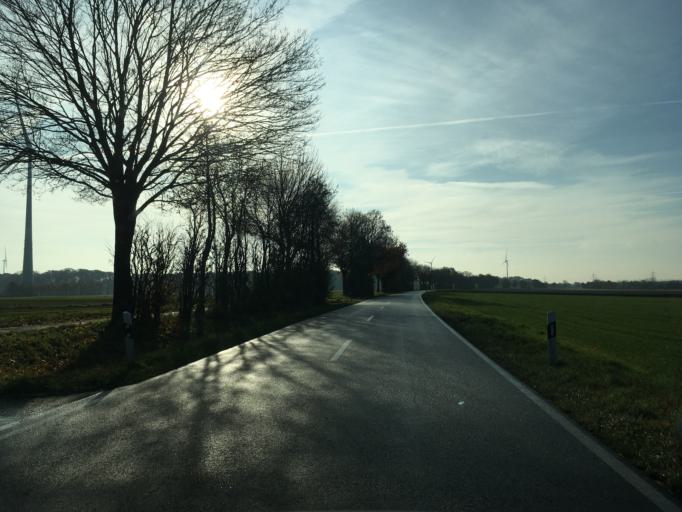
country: DE
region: North Rhine-Westphalia
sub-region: Regierungsbezirk Munster
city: Ahaus
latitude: 52.0545
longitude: 6.9836
